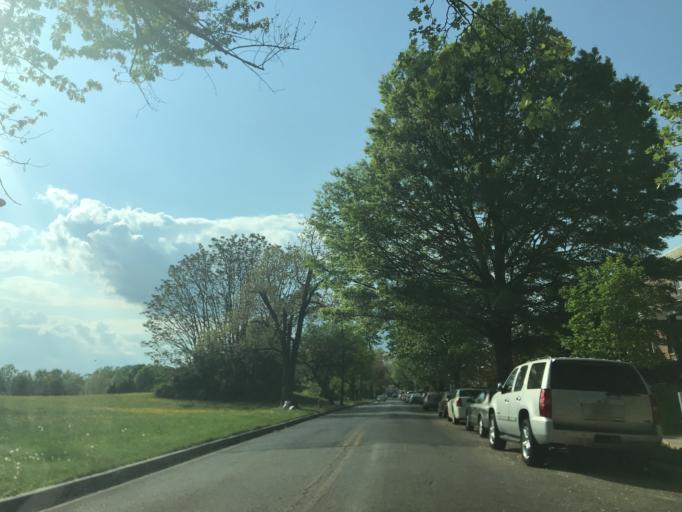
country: US
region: Maryland
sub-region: Baltimore County
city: Rosedale
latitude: 39.3260
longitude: -76.5637
